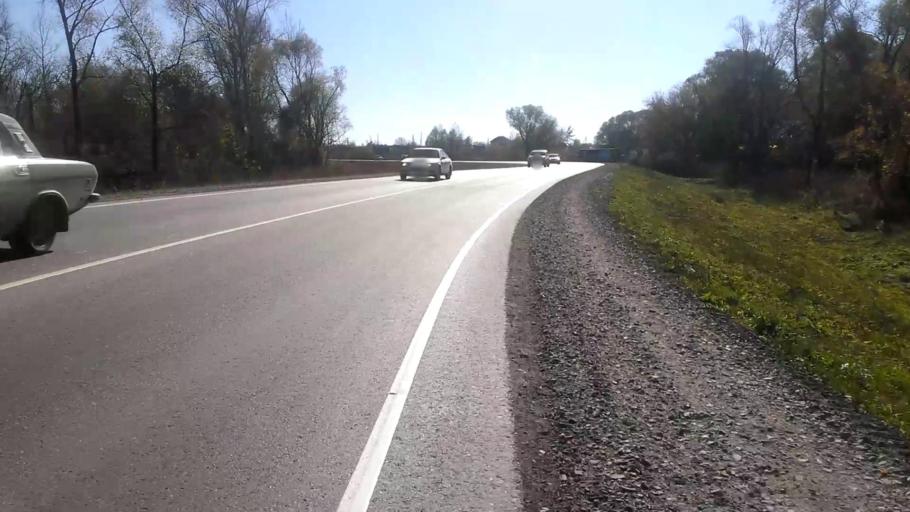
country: RU
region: Altai Krai
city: Sannikovo
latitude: 53.3230
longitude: 83.9429
